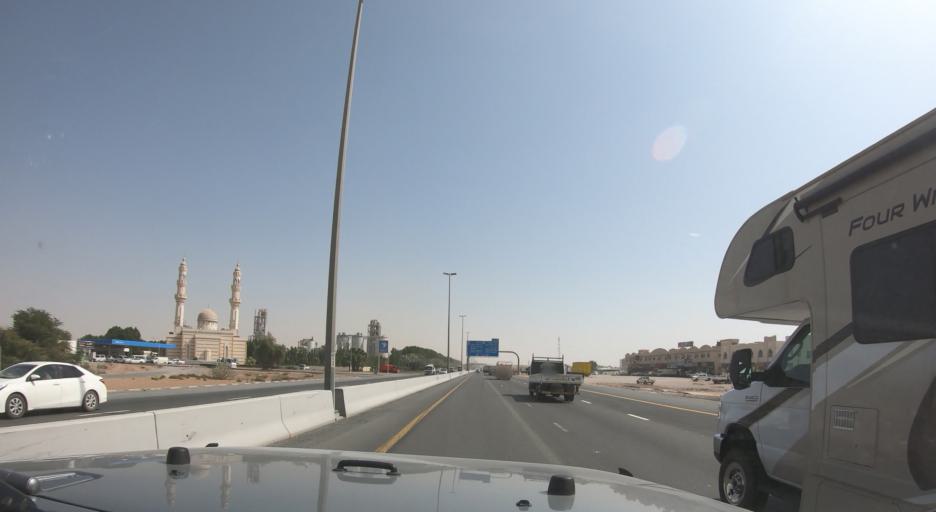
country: AE
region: Ash Shariqah
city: Sharjah
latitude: 25.2964
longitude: 55.6087
